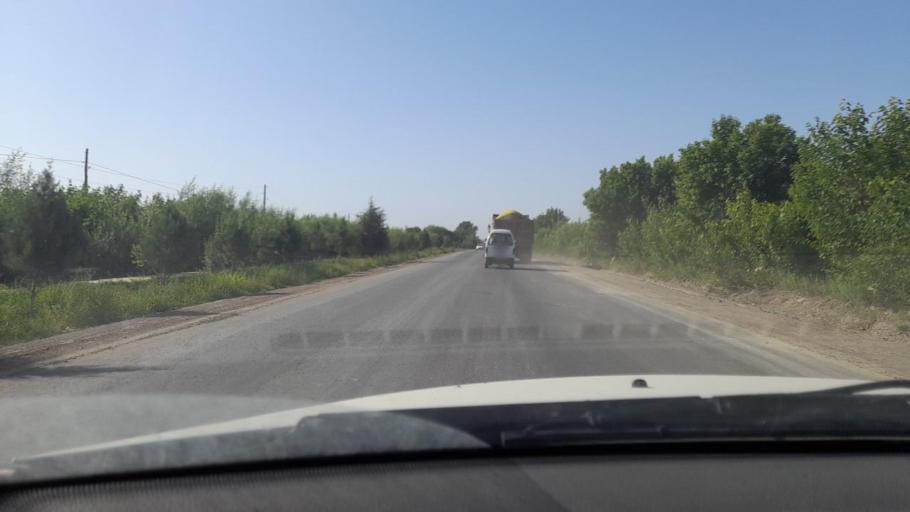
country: UZ
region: Bukhara
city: Romiton
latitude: 40.0523
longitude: 64.3283
